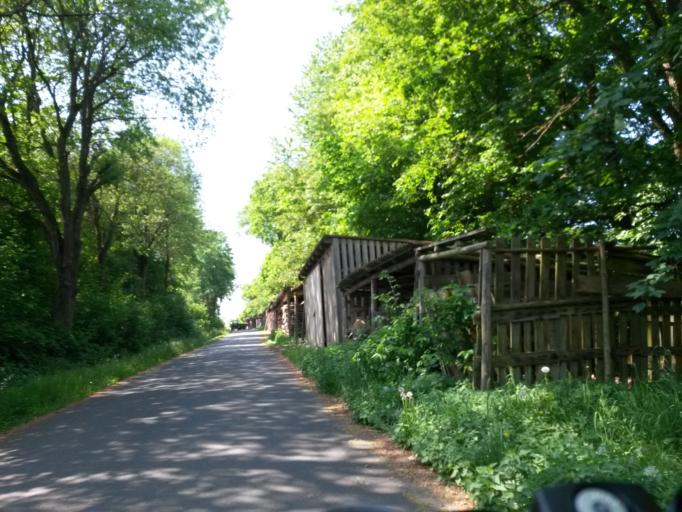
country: DE
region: Bavaria
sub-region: Regierungsbezirk Unterfranken
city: Euerdorf
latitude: 50.1604
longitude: 10.0024
